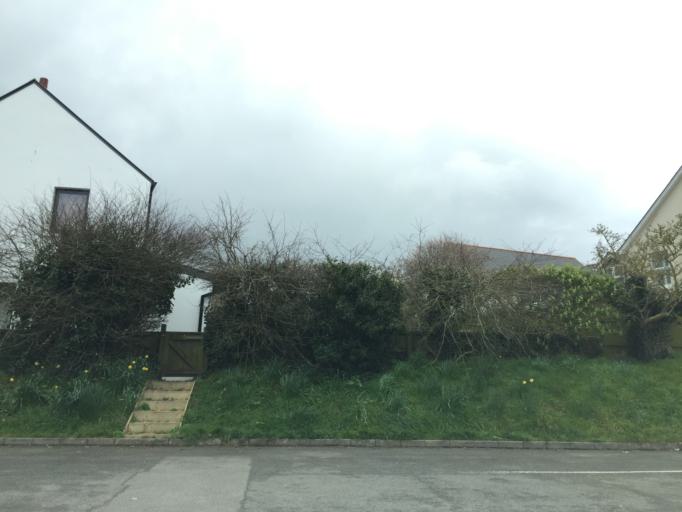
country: JE
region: St Helier
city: Saint Helier
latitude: 49.2357
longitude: -2.1728
